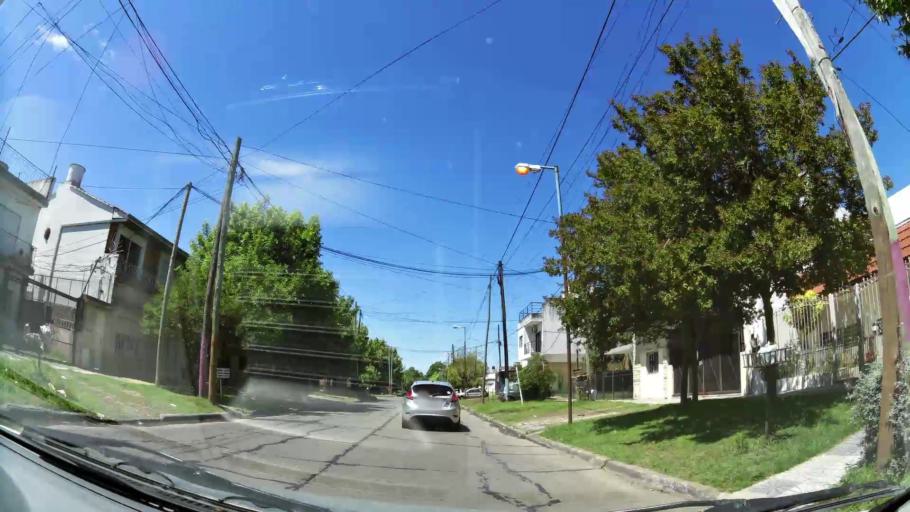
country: AR
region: Buenos Aires
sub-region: Partido de Quilmes
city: Quilmes
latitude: -34.7243
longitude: -58.2755
